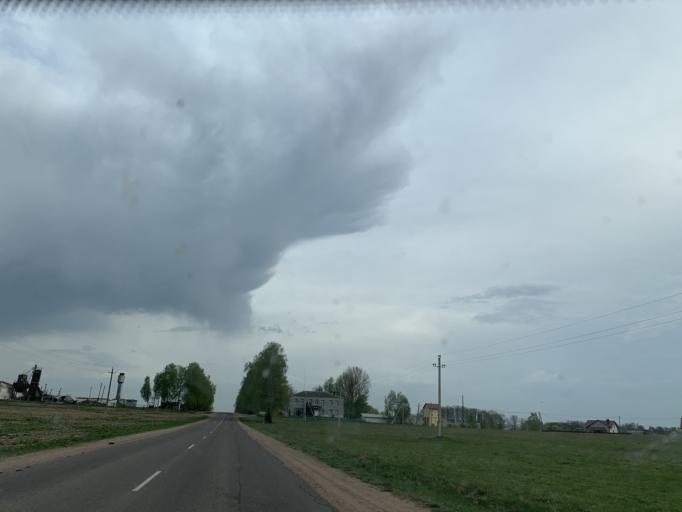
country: BY
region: Minsk
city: Kapyl'
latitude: 53.2656
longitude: 26.9572
